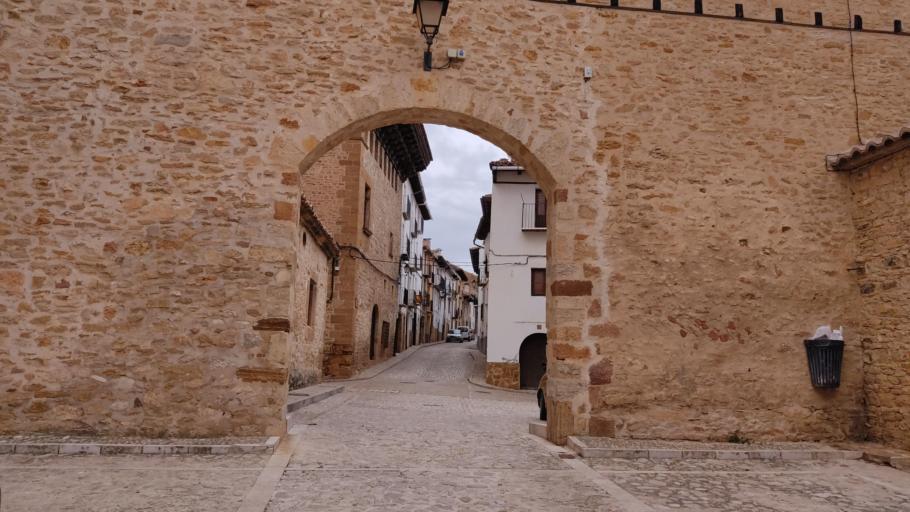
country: ES
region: Aragon
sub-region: Provincia de Teruel
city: La Iglesuela del Cid
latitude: 40.4820
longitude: -0.3184
